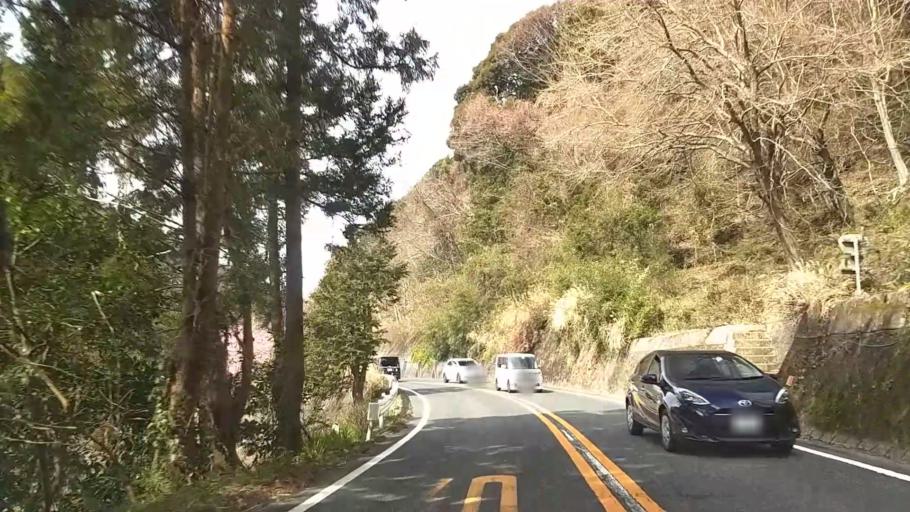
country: JP
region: Shizuoka
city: Shimoda
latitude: 34.7859
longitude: 138.9458
